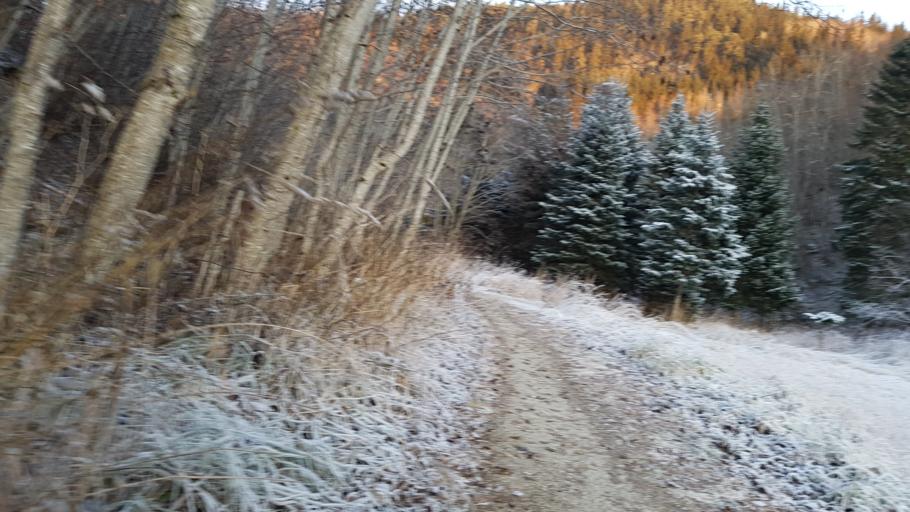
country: NO
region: Sor-Trondelag
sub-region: Melhus
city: Melhus
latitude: 63.2745
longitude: 10.2992
